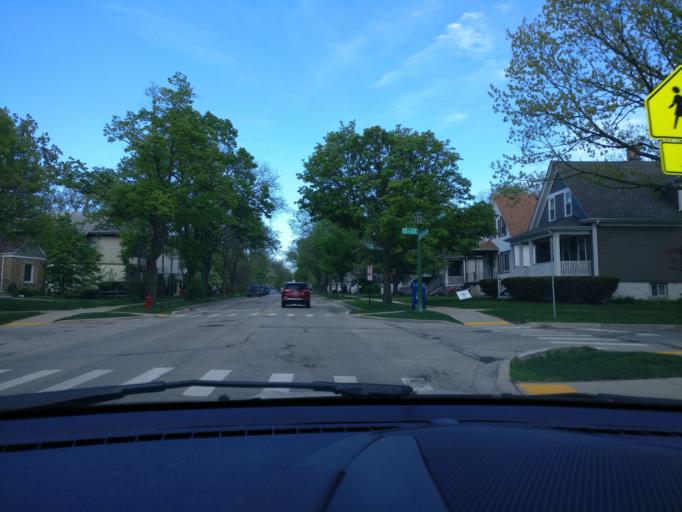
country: US
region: Illinois
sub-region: Cook County
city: Wilmette
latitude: 42.0727
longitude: -87.7148
